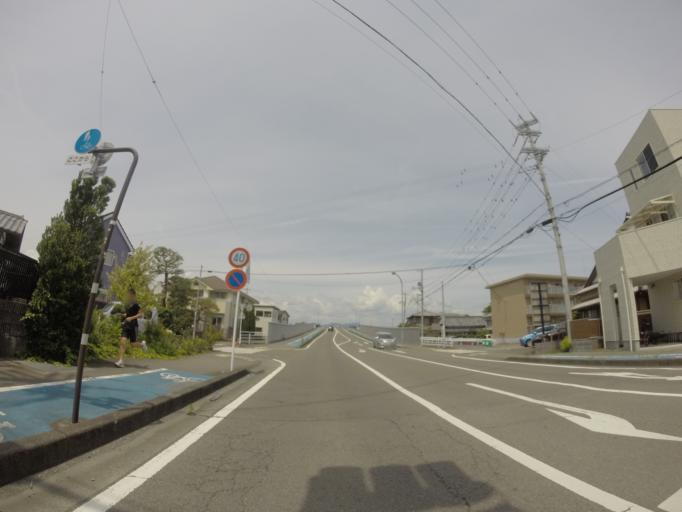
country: JP
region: Shizuoka
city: Fujieda
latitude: 34.8657
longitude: 138.2832
